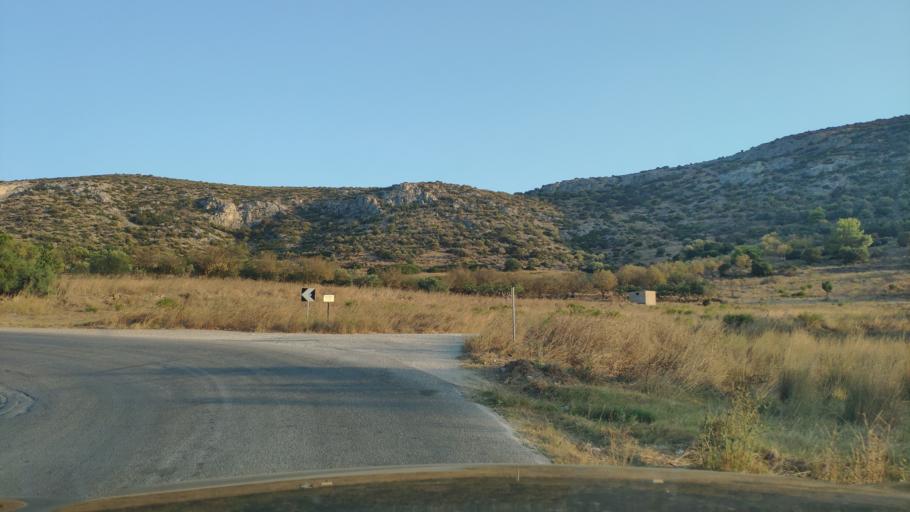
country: GR
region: Attica
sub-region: Nomarchia Anatolikis Attikis
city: Limin Mesoyaias
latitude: 37.9220
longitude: 23.9945
